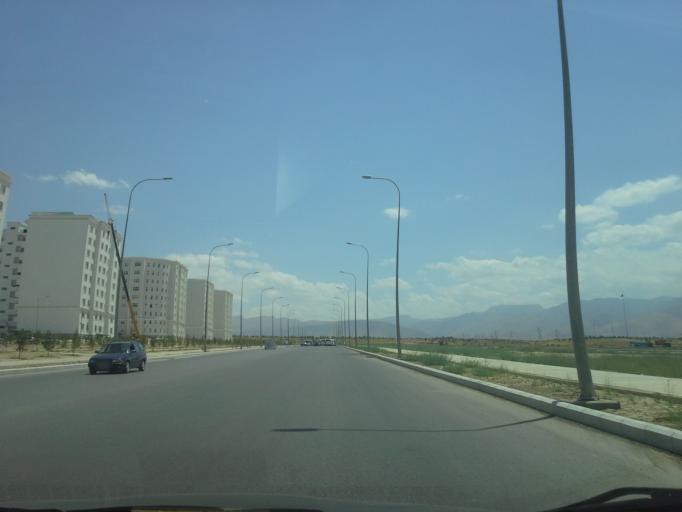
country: TM
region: Ahal
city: Ashgabat
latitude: 37.8899
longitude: 58.4055
